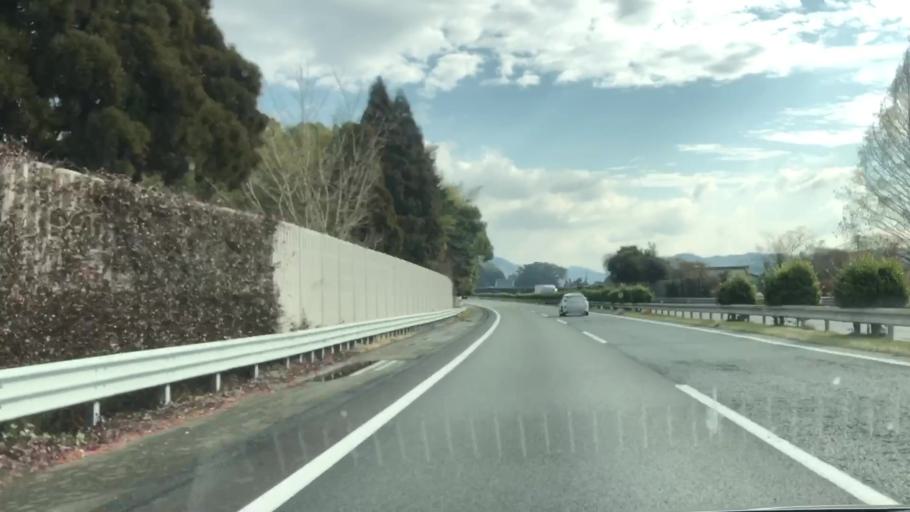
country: JP
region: Fukuoka
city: Setakamachi-takayanagi
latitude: 33.1226
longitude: 130.5200
